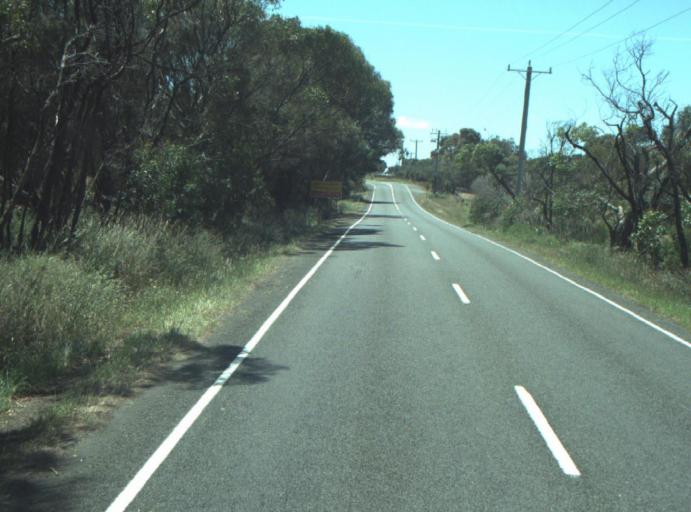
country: AU
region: Victoria
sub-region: Greater Geelong
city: Clifton Springs
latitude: -38.2443
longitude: 144.5709
